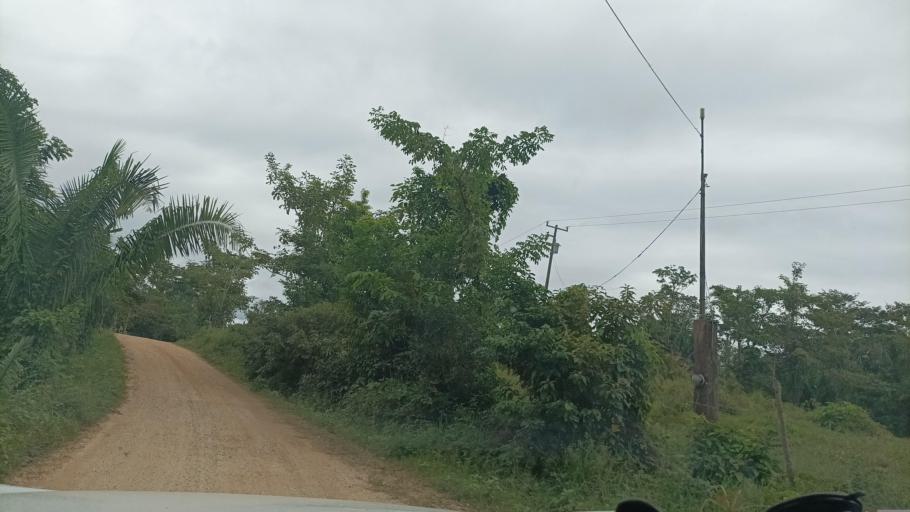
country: MX
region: Veracruz
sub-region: Uxpanapa
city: Poblado Cinco
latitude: 17.4907
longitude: -94.5708
